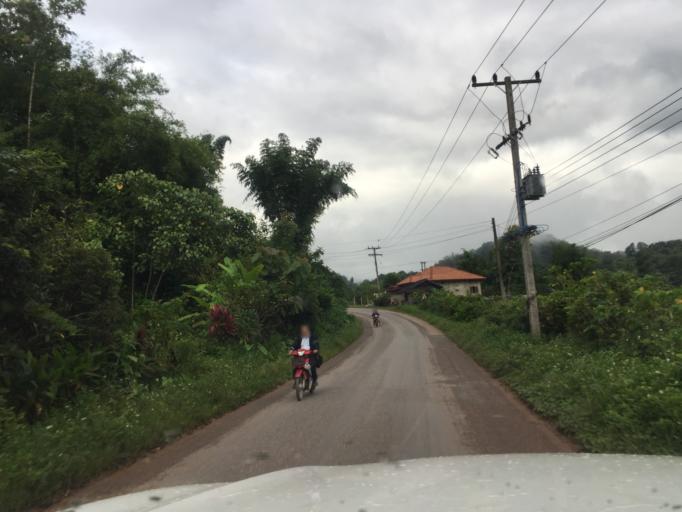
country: LA
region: Oudomxai
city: Muang La
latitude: 20.8576
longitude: 102.1121
